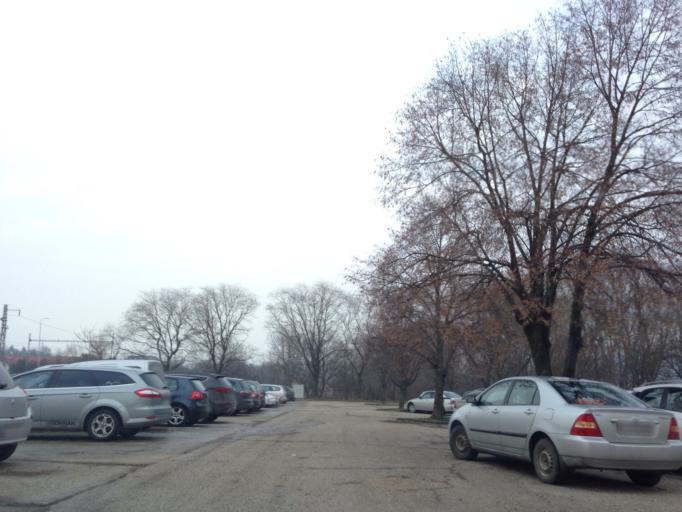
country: SK
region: Nitriansky
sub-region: Okres Nitra
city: Vrable
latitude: 48.1007
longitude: 18.3385
